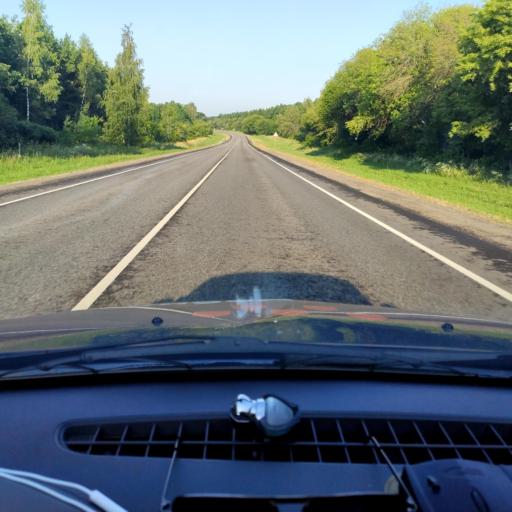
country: RU
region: Lipetsk
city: Izmalkovo
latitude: 52.4481
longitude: 37.9828
